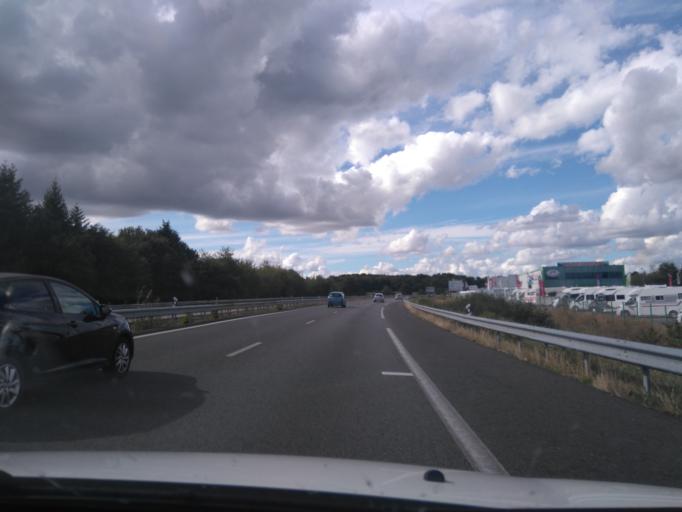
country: FR
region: Brittany
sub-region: Departement d'Ille-et-Vilaine
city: Laille
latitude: 47.9622
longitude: -1.6876
